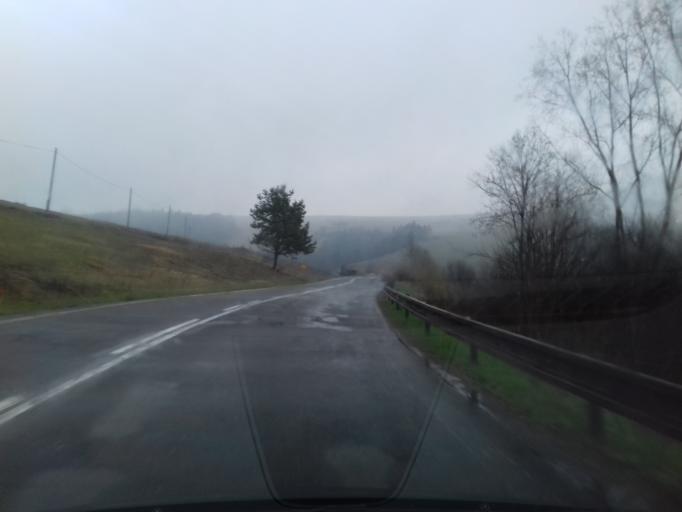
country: SK
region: Presovsky
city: Stara L'ubovna
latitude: 49.3570
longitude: 20.6926
